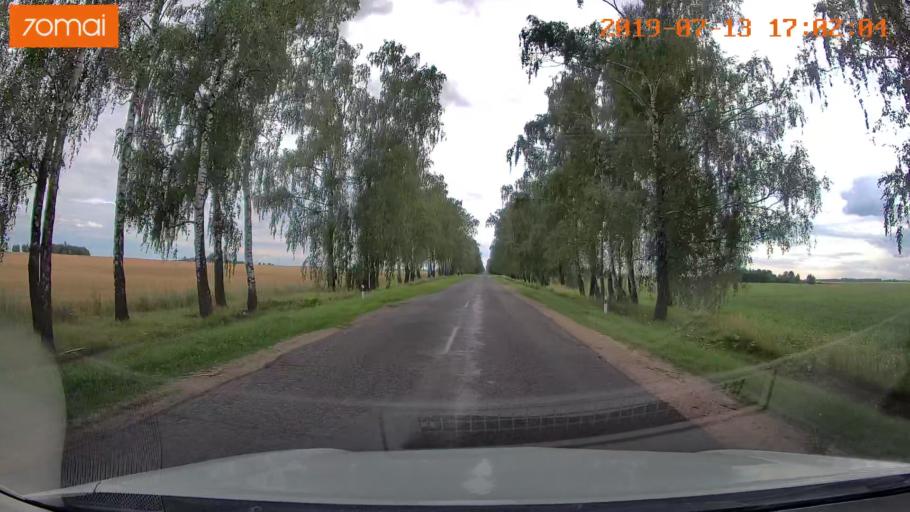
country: BY
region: Mogilev
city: Kirawsk
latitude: 53.2897
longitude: 29.3906
